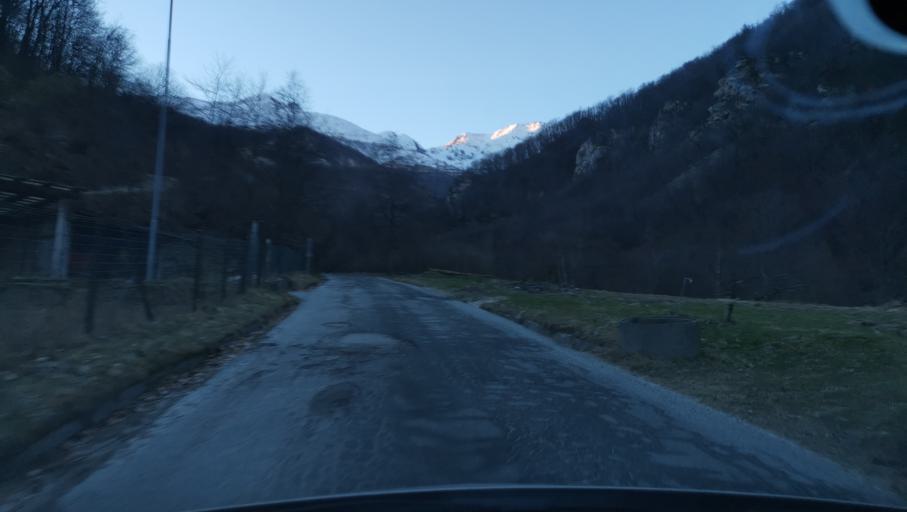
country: IT
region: Piedmont
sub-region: Provincia di Torino
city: Rora
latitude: 44.7734
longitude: 7.2054
